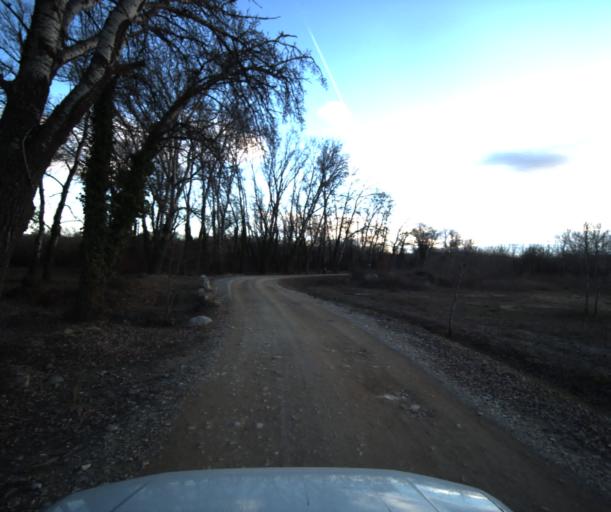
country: FR
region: Provence-Alpes-Cote d'Azur
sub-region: Departement du Vaucluse
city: Pertuis
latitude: 43.6699
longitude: 5.5037
